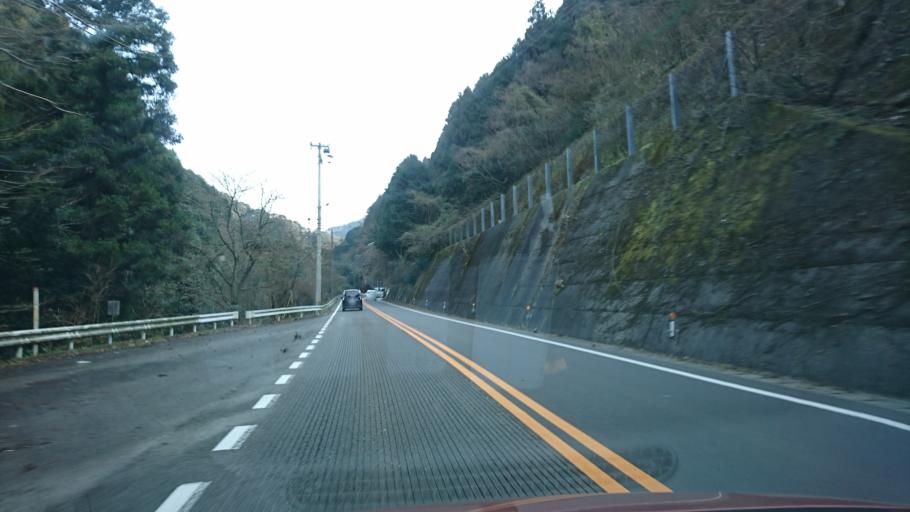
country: JP
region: Ehime
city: Hojo
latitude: 33.9621
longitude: 132.9075
